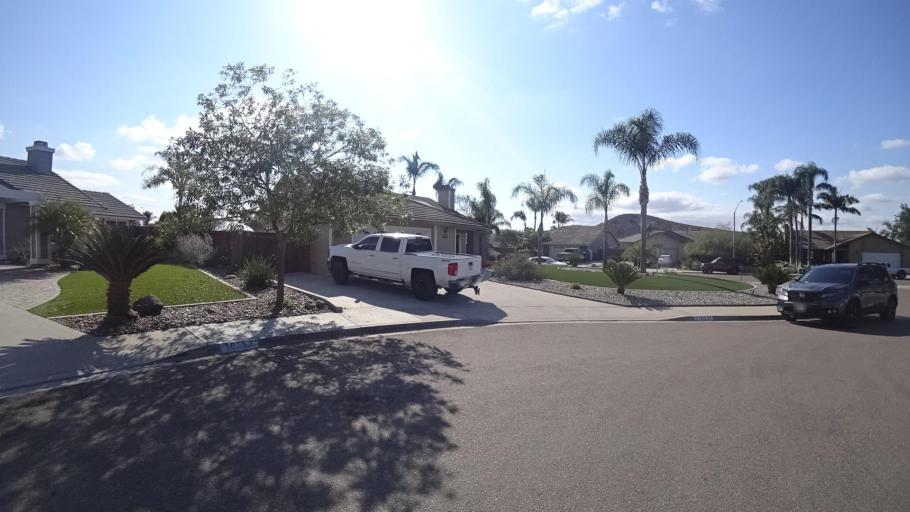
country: US
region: California
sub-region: San Diego County
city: Eucalyptus Hills
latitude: 32.8618
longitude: -116.9587
